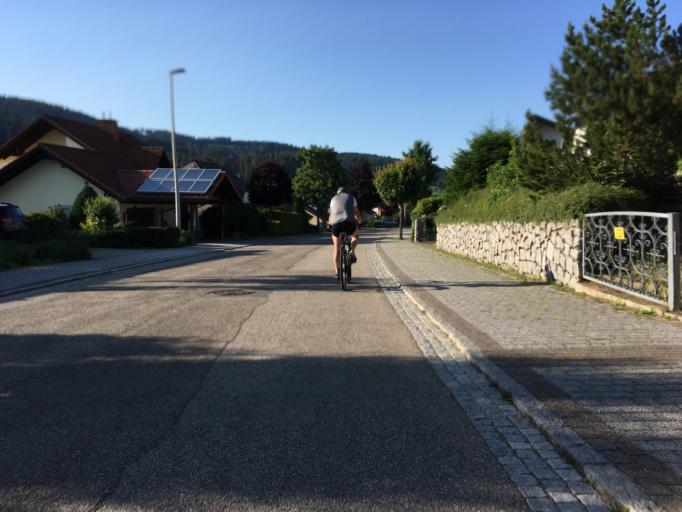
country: DE
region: Baden-Wuerttemberg
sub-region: Freiburg Region
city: Titisee-Neustadt
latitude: 47.9199
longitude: 8.2194
